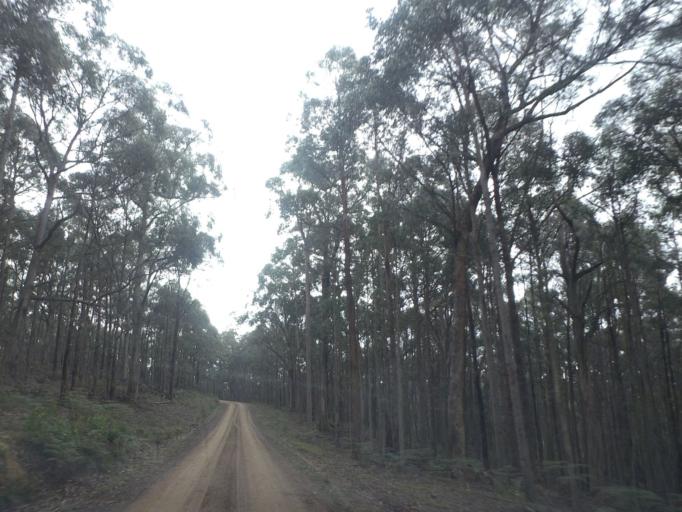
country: AU
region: Victoria
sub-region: Moorabool
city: Bacchus Marsh
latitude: -37.4350
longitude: 144.3182
